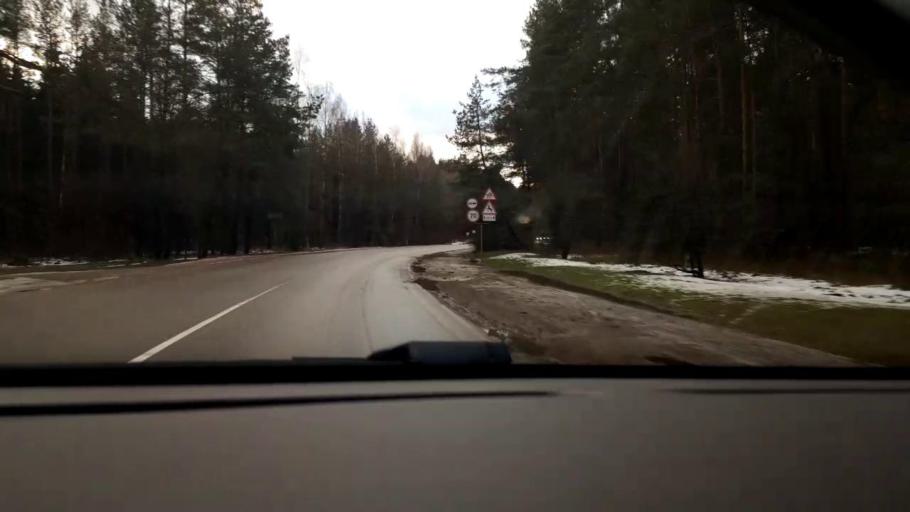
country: LT
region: Vilnius County
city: Rasos
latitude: 54.7749
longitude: 25.3840
